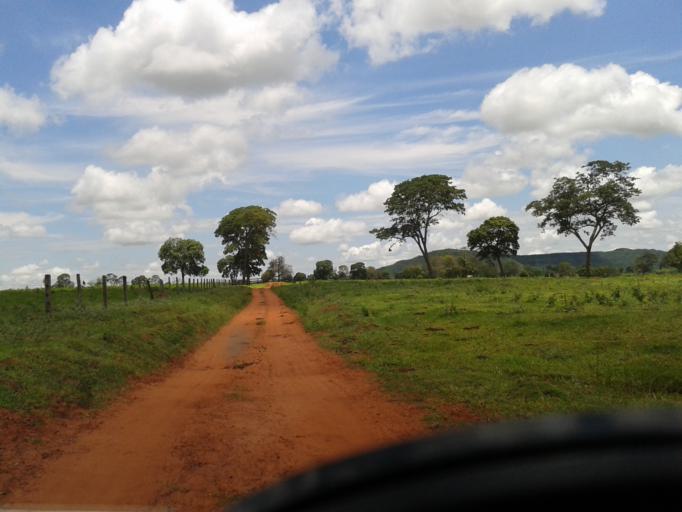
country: BR
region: Minas Gerais
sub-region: Santa Vitoria
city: Santa Vitoria
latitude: -19.0036
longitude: -49.9194
